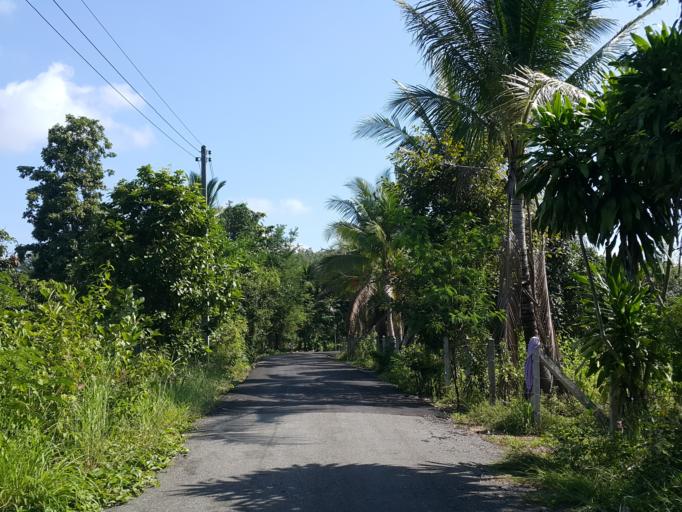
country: TH
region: Chiang Mai
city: Mae On
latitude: 18.8091
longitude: 99.1824
